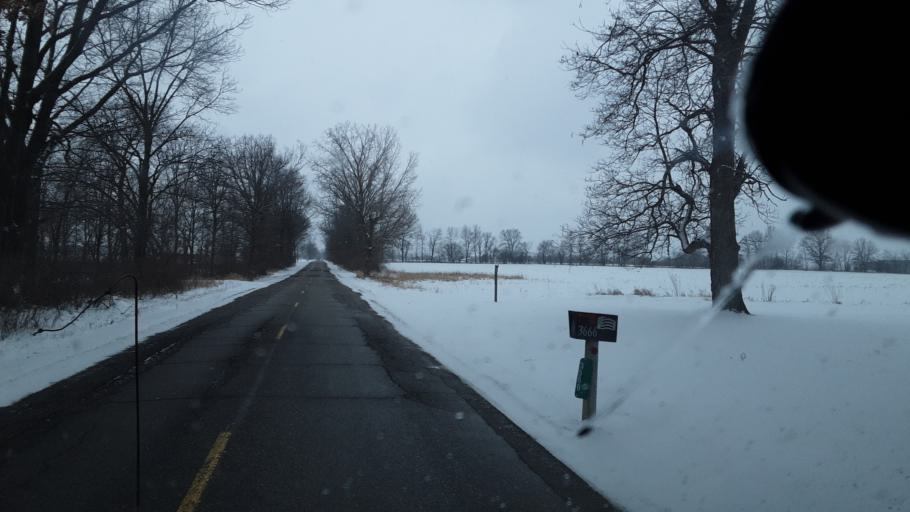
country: US
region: Michigan
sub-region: Ingham County
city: Leslie
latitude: 42.4756
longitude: -84.3941
